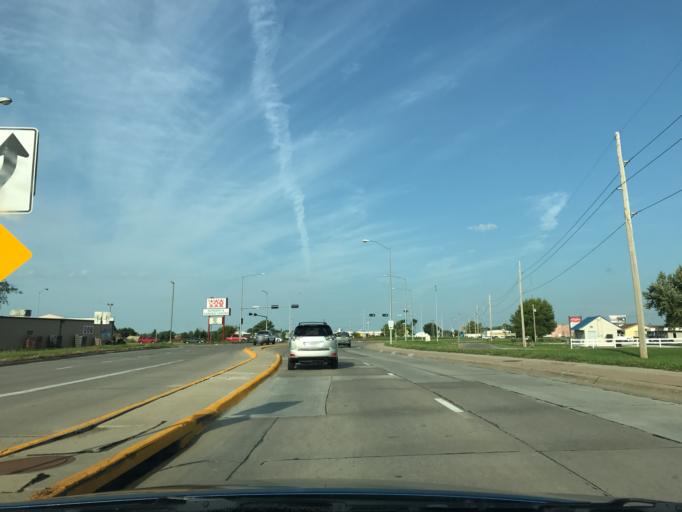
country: US
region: Nebraska
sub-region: Platte County
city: Columbus
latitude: 41.4388
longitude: -97.3810
